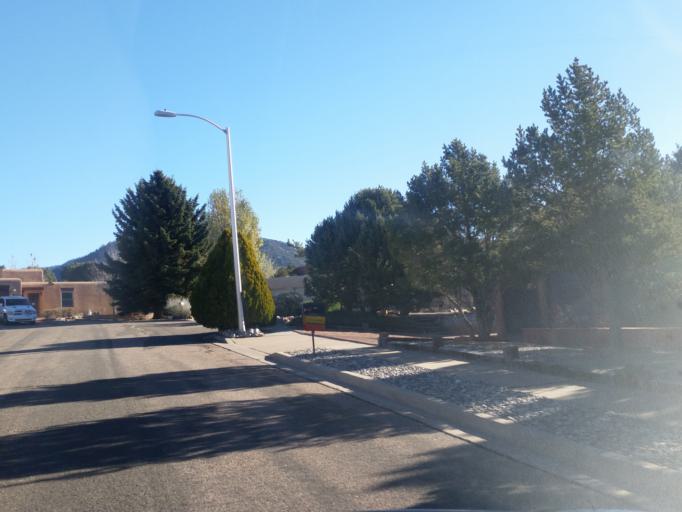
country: US
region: New Mexico
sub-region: Santa Fe County
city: Santa Fe
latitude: 35.6468
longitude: -105.9320
